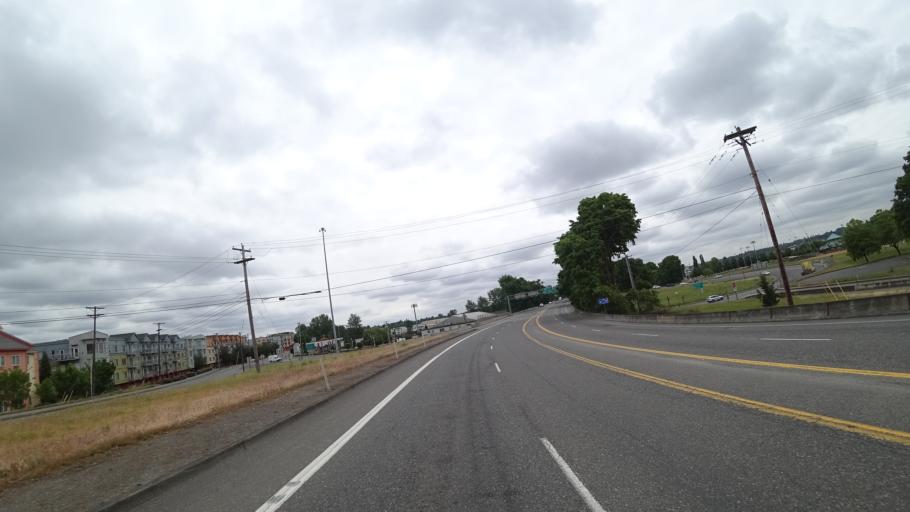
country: US
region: Washington
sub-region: Clark County
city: Vancouver
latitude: 45.6032
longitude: -122.6801
